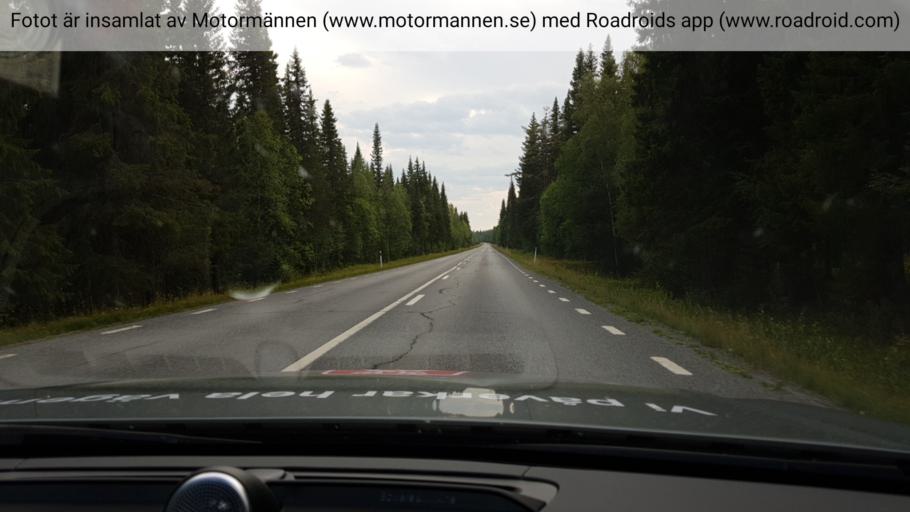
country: SE
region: Jaemtland
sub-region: Stroemsunds Kommun
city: Stroemsund
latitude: 63.5237
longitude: 15.3165
